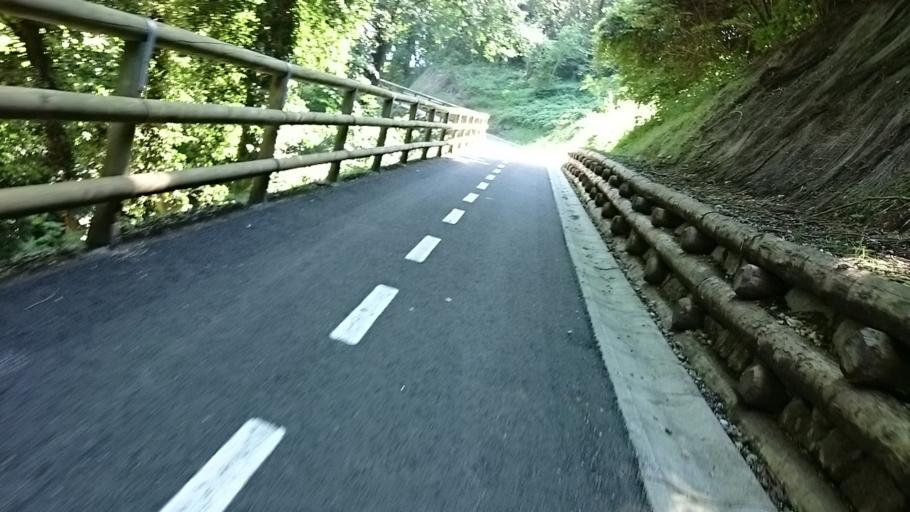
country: IT
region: Veneto
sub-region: Provincia di Belluno
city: Castello Lavazzo
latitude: 46.2830
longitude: 12.3087
